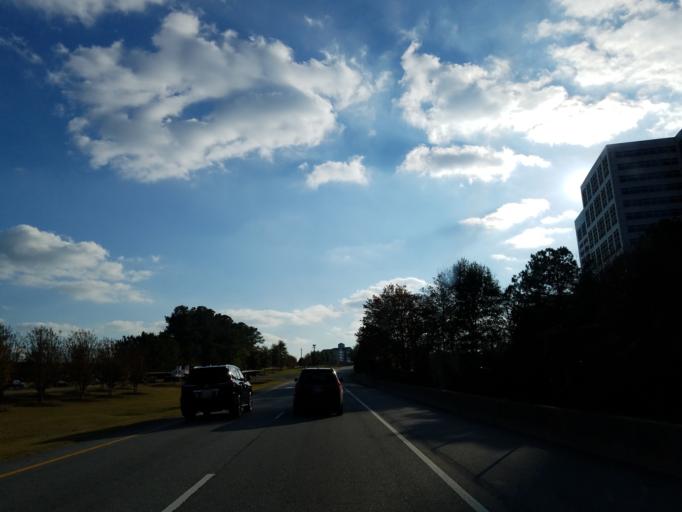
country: US
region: Georgia
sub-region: Cobb County
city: Vinings
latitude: 33.8668
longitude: -84.4793
